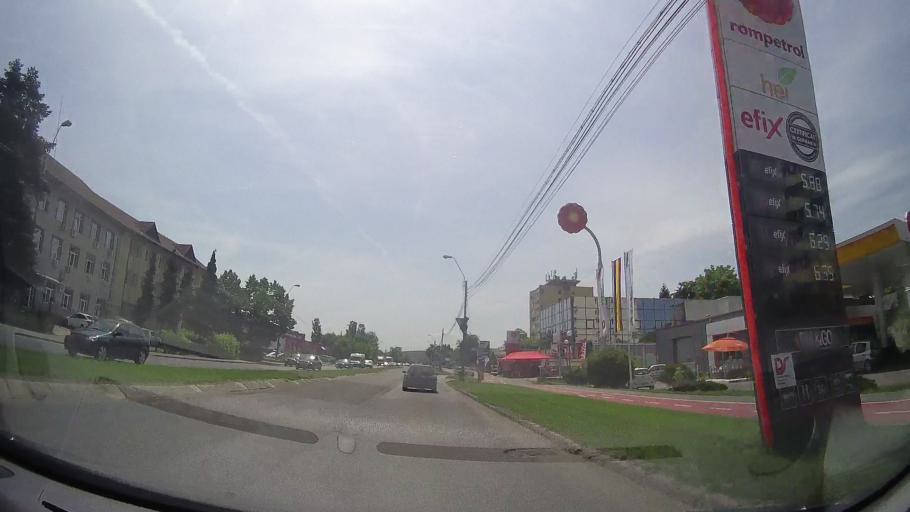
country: RO
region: Hunedoara
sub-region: Municipiul Deva
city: Deva
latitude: 45.8766
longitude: 22.9153
